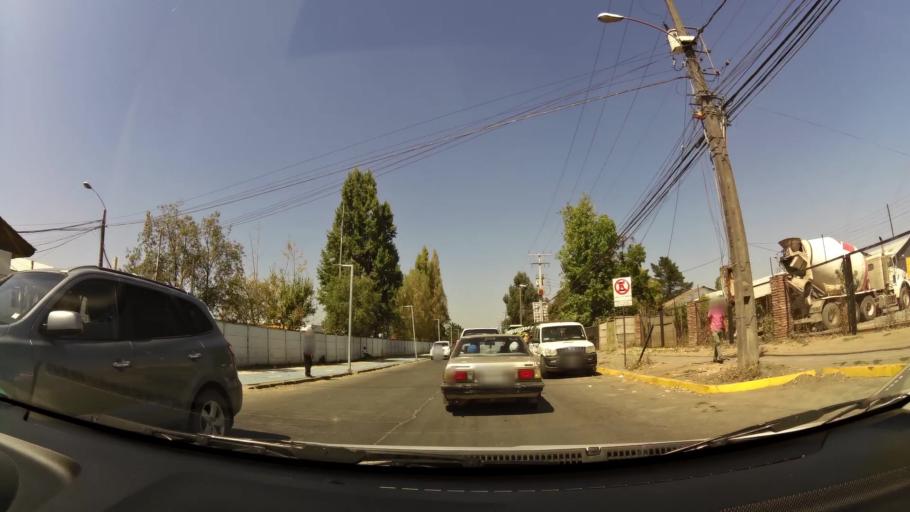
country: CL
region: Maule
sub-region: Provincia de Talca
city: Talca
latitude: -35.4210
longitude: -71.6362
